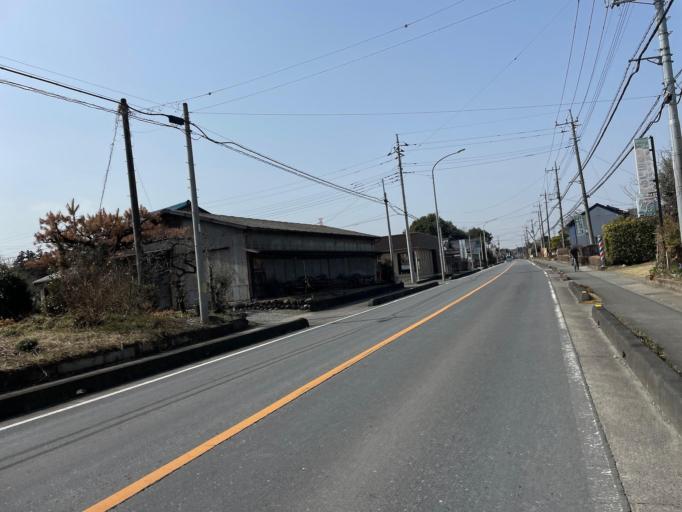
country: JP
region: Saitama
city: Ogawa
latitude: 36.1015
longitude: 139.2713
